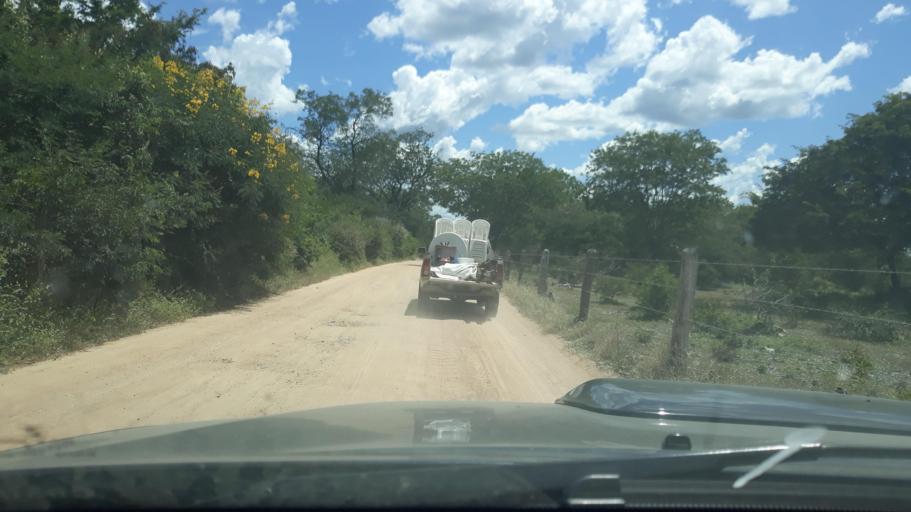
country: BR
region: Bahia
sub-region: Riacho De Santana
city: Riacho de Santana
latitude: -13.9099
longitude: -42.9392
